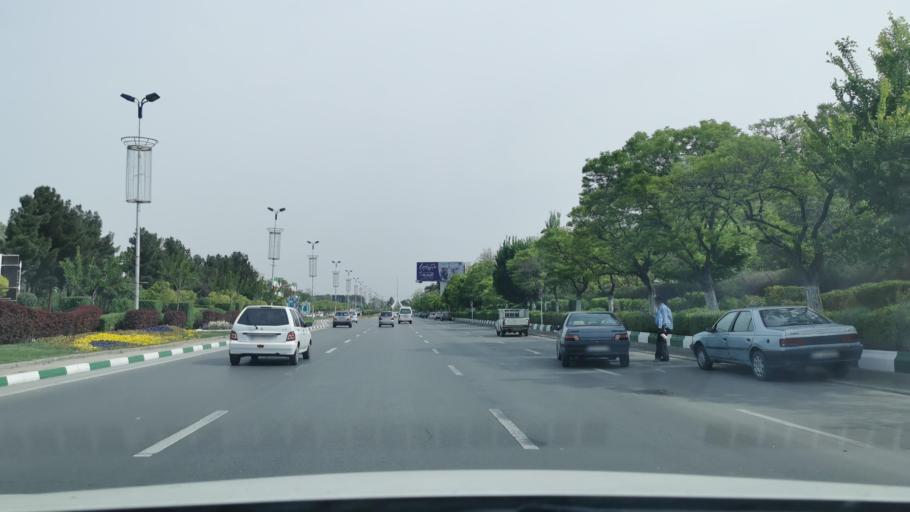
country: IR
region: Razavi Khorasan
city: Mashhad
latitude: 36.2479
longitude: 59.6188
